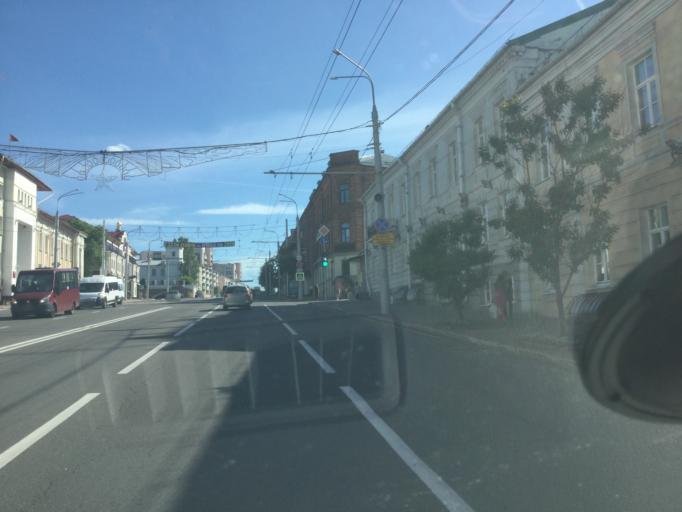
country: BY
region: Vitebsk
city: Vitebsk
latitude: 55.1896
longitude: 30.2056
